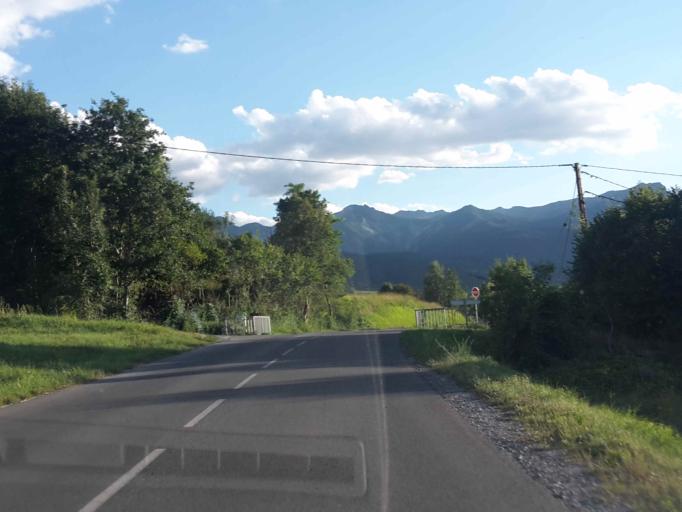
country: FR
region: Provence-Alpes-Cote d'Azur
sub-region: Departement des Hautes-Alpes
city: Embrun
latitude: 44.5522
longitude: 6.5042
